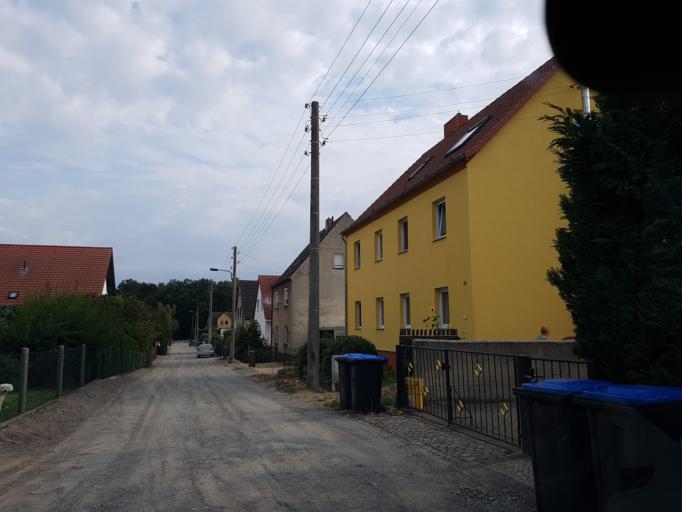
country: DE
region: Saxony-Anhalt
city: Wittenburg
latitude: 51.8933
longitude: 12.6232
